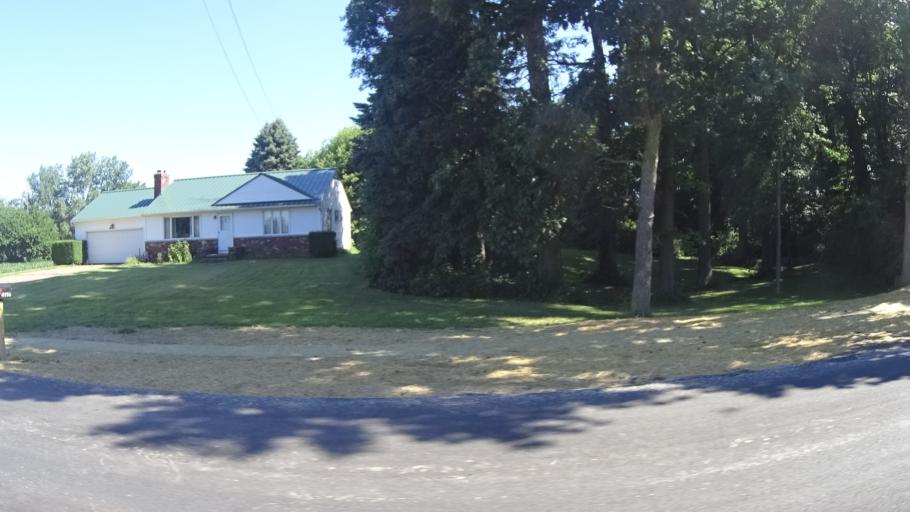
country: US
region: Ohio
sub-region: Erie County
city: Huron
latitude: 41.3953
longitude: -82.6382
